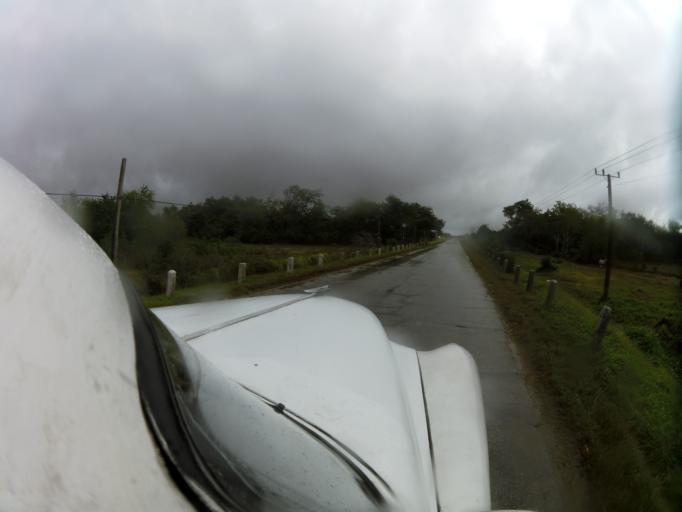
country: CU
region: Las Tunas
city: Las Tunas
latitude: 20.9202
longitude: -76.8521
